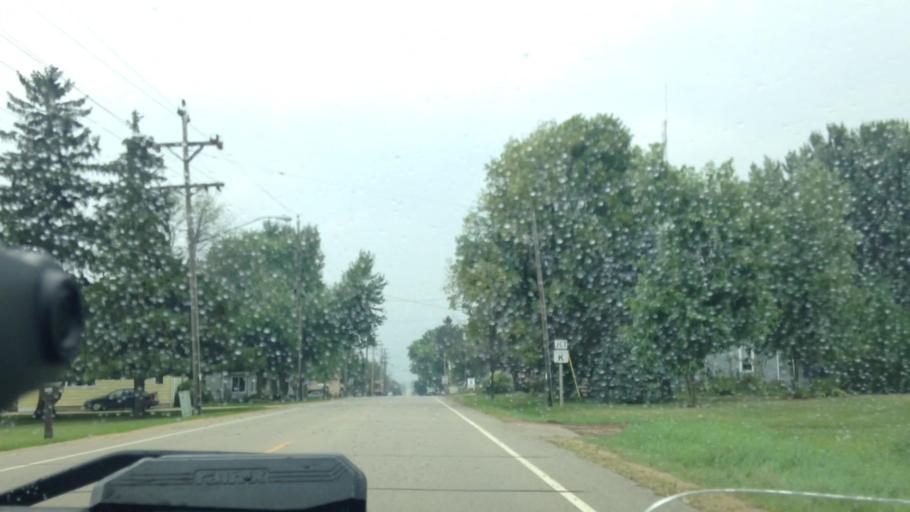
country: US
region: Wisconsin
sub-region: Washington County
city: Slinger
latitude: 43.3725
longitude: -88.3360
